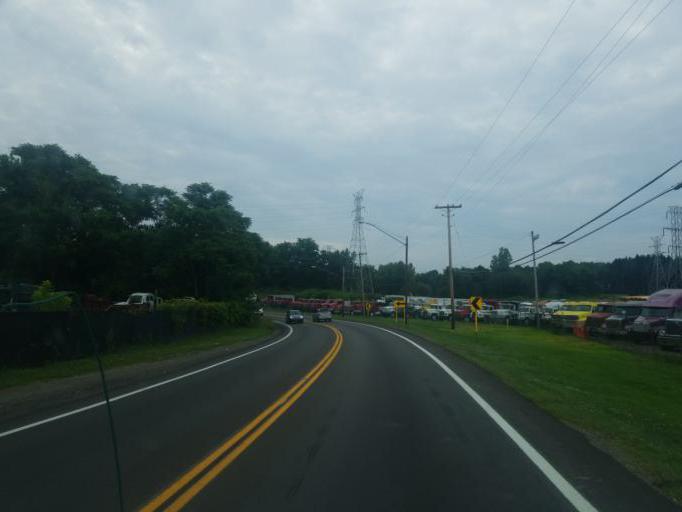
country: US
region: Ohio
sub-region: Stark County
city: Canton
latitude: 40.7745
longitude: -81.3466
